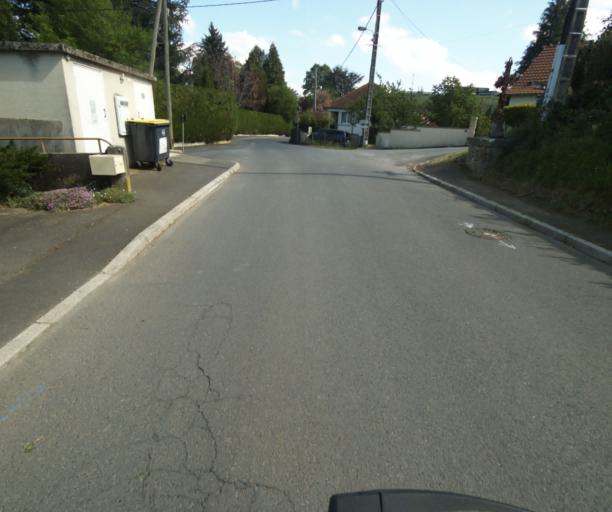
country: FR
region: Limousin
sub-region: Departement de la Correze
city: Tulle
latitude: 45.2635
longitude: 1.7789
